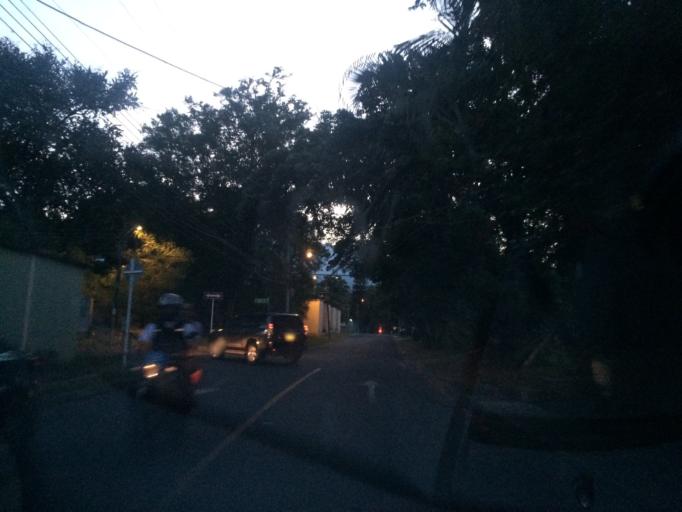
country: CO
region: Valle del Cauca
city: Cali
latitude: 3.3633
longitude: -76.5344
